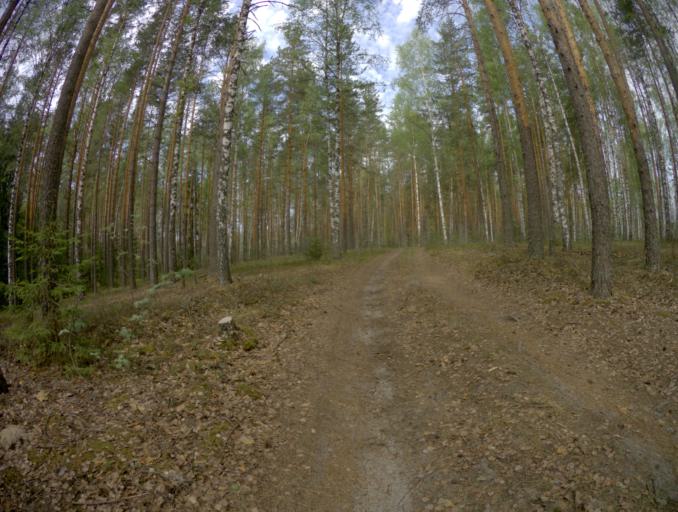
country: RU
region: Ivanovo
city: Talitsy
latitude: 56.4844
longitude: 42.1611
